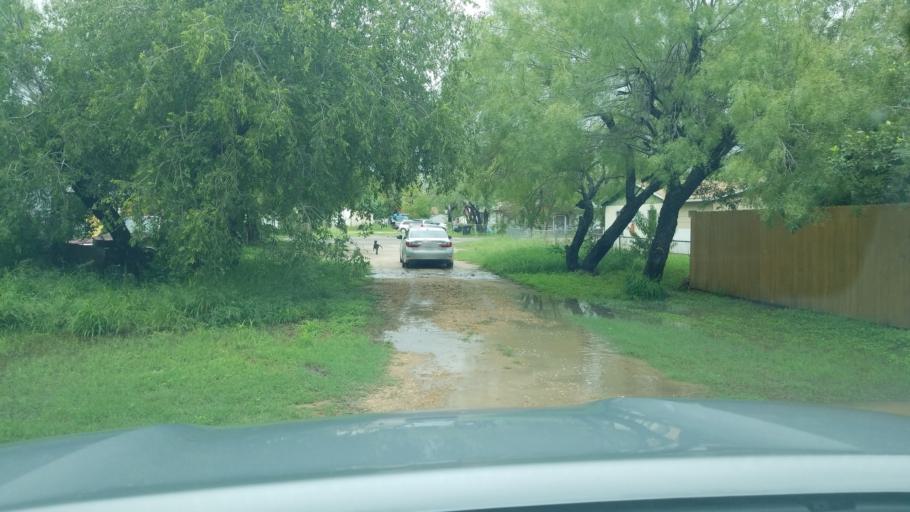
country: US
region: Texas
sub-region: Dimmit County
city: Carrizo Springs
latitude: 28.5307
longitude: -99.8473
